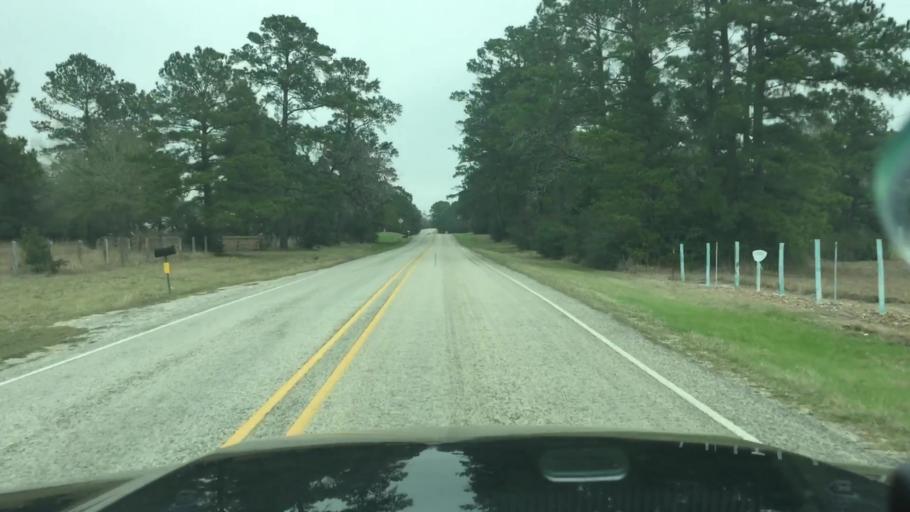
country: US
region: Texas
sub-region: Fayette County
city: La Grange
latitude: 30.0107
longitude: -96.9392
